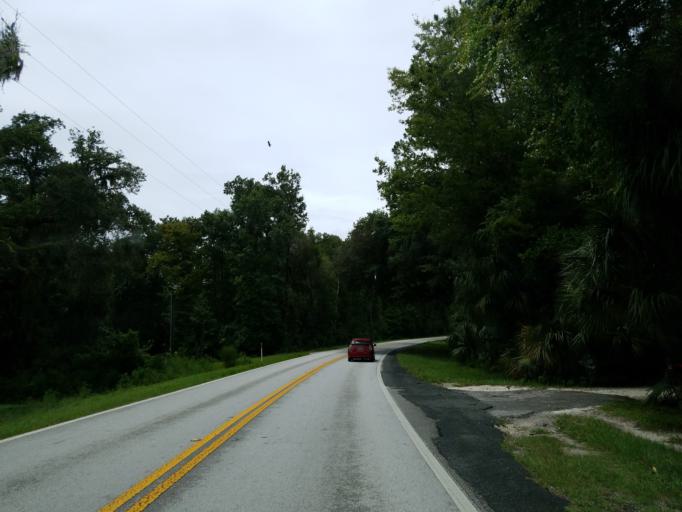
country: US
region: Florida
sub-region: Sumter County
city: Bushnell
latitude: 28.6910
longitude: -82.2082
